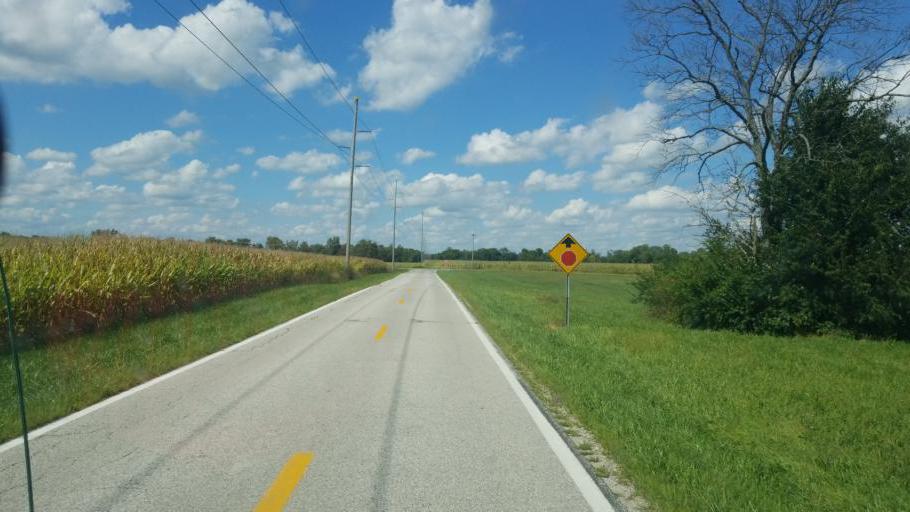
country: US
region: Ohio
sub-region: Marion County
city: Prospect
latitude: 40.3299
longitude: -83.2044
